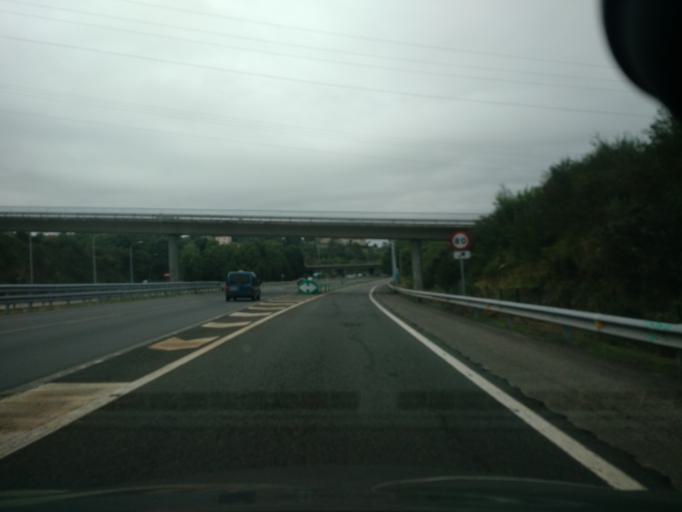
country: ES
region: Galicia
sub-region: Provincia da Coruna
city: Santiago de Compostela
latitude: 42.8922
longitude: -8.5042
